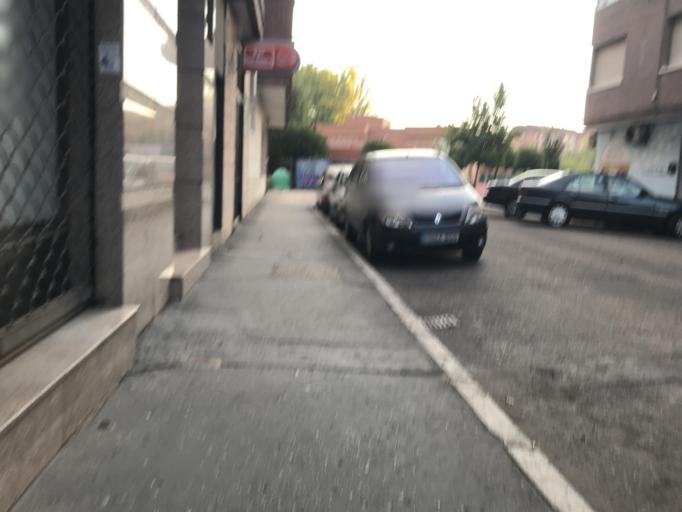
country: ES
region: Castille and Leon
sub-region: Provincia de Valladolid
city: Valladolid
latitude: 41.6556
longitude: -4.7135
